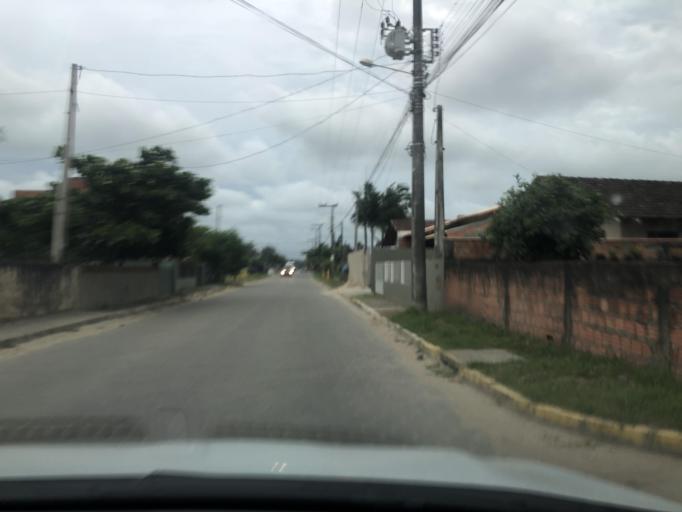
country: BR
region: Santa Catarina
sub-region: Sao Francisco Do Sul
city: Sao Francisco do Sul
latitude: -26.2284
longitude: -48.5250
